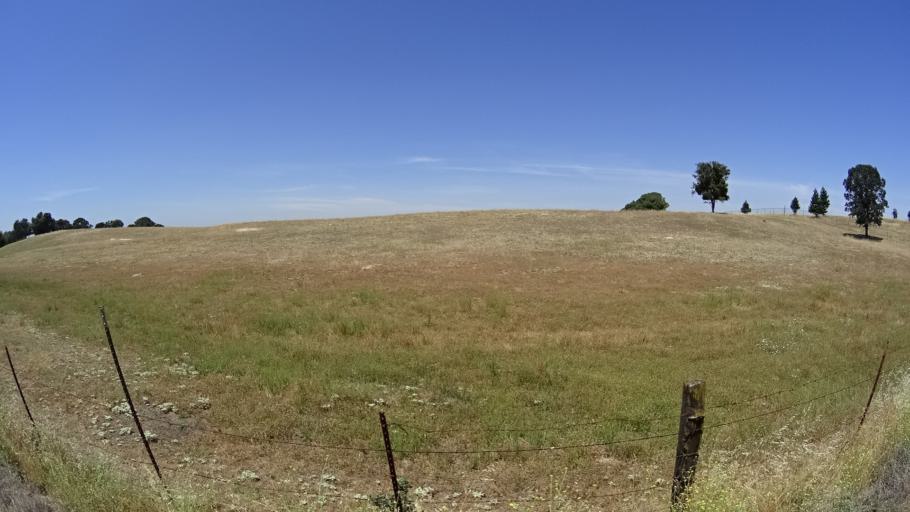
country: US
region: California
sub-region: Calaveras County
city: Rancho Calaveras
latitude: 38.1407
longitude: -120.9133
